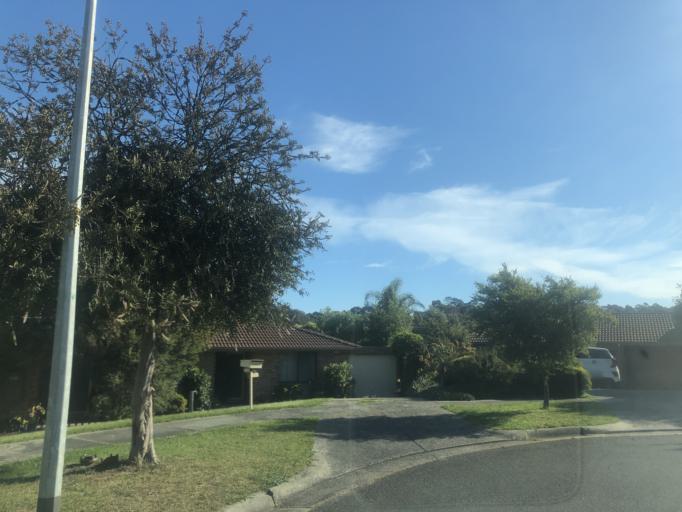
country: AU
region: Victoria
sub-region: Monash
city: Mulgrave
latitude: -37.9204
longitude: 145.1978
